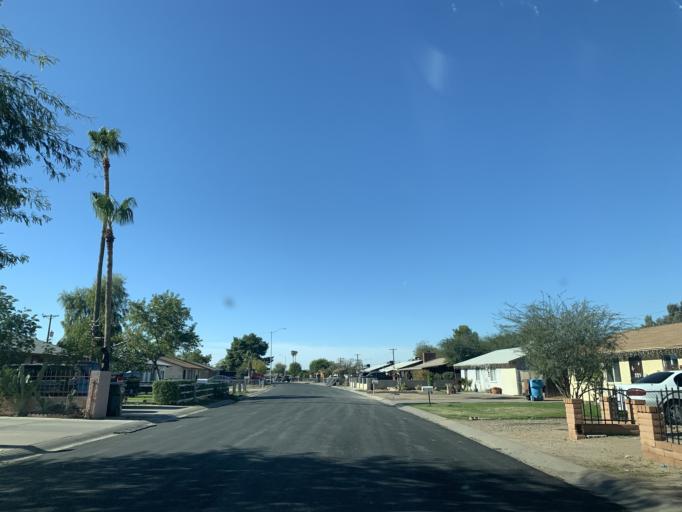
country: US
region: Arizona
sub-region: Maricopa County
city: Laveen
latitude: 33.3906
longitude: -112.1432
